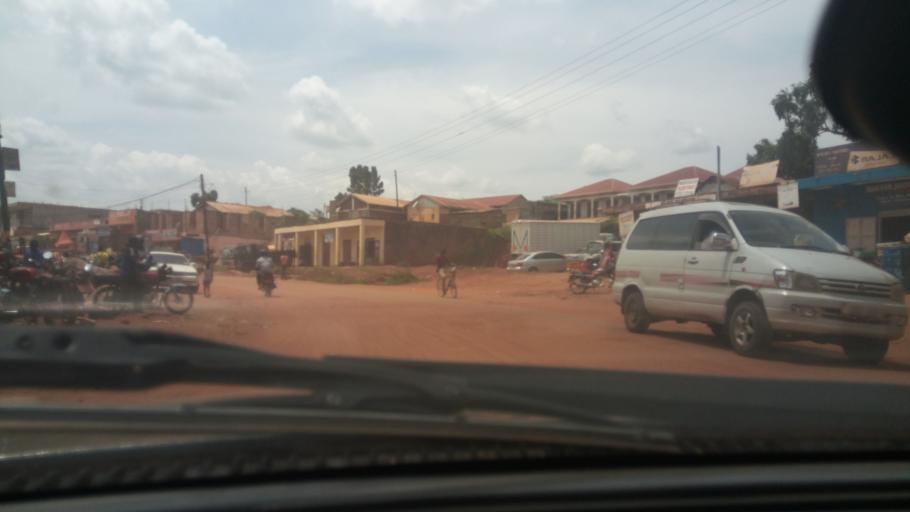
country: UG
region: Central Region
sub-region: Mityana District
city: Mityana
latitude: 0.4027
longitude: 32.0444
